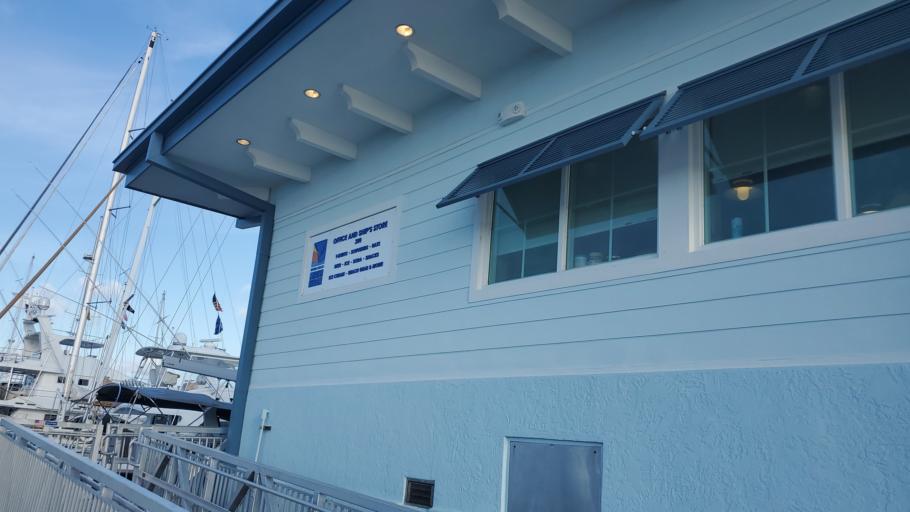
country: US
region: Florida
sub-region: Palm Beach County
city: Riviera Beach
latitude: 26.7728
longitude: -80.0504
